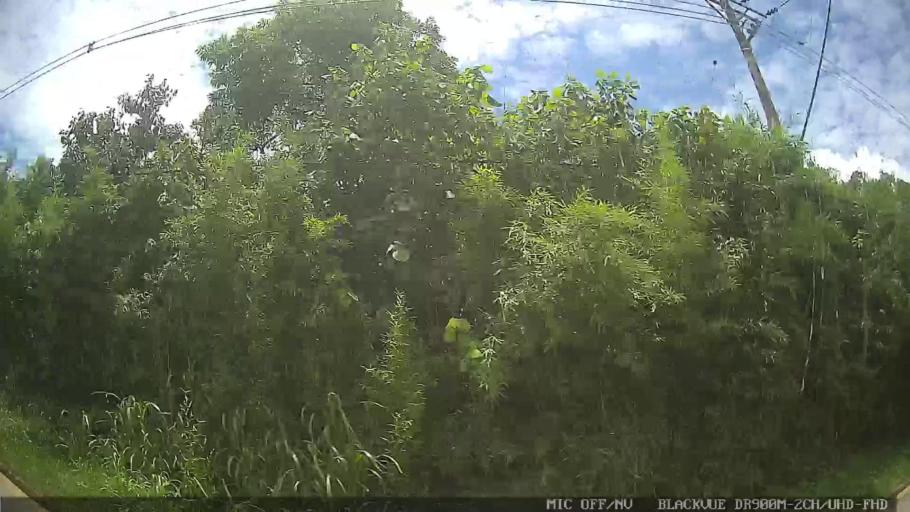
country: BR
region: Sao Paulo
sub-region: Biritiba-Mirim
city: Biritiba Mirim
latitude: -23.5565
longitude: -45.9870
